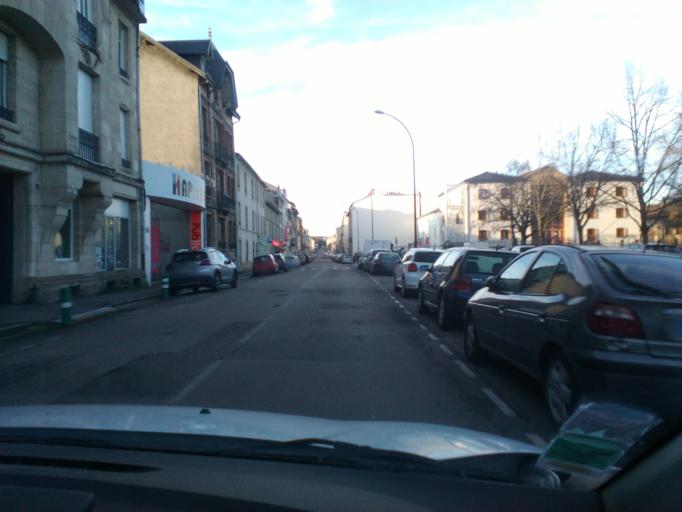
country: FR
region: Lorraine
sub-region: Departement des Vosges
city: Epinal
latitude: 48.1799
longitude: 6.4456
